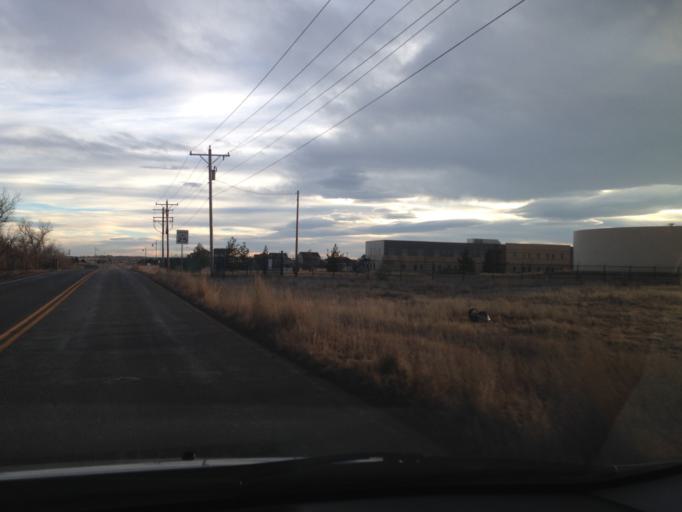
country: US
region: Colorado
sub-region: Weld County
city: Dacono
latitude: 40.0982
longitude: -104.9989
